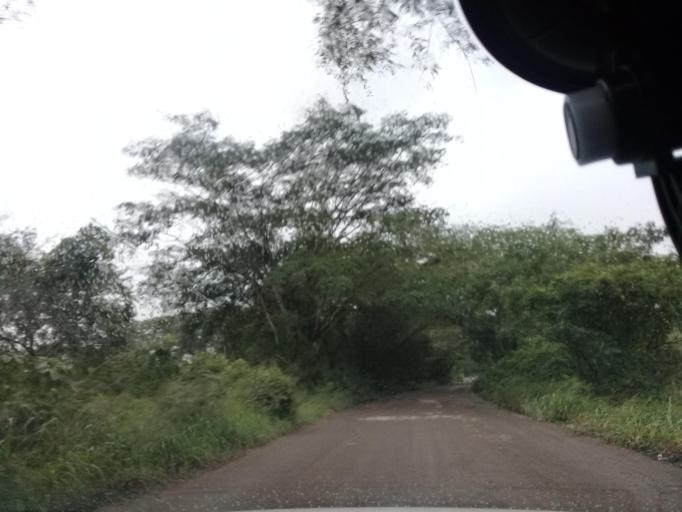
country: MX
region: Veracruz
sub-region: Chalma
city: San Pedro Coyutla
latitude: 21.2216
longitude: -98.3821
